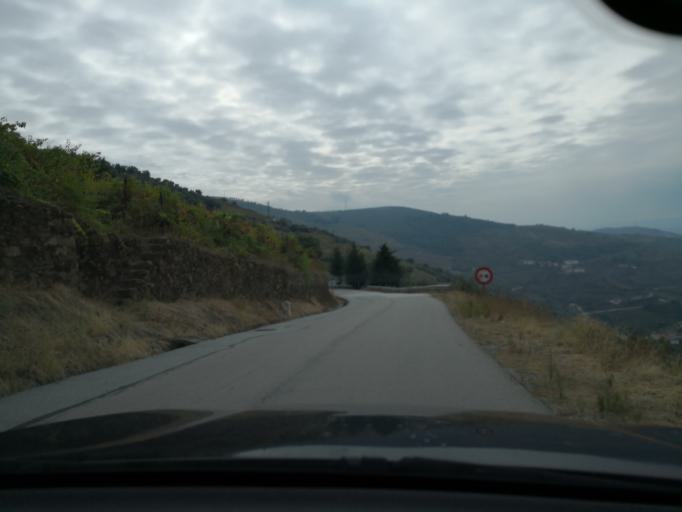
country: PT
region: Vila Real
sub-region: Peso da Regua
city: Peso da Regua
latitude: 41.1846
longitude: -7.7415
